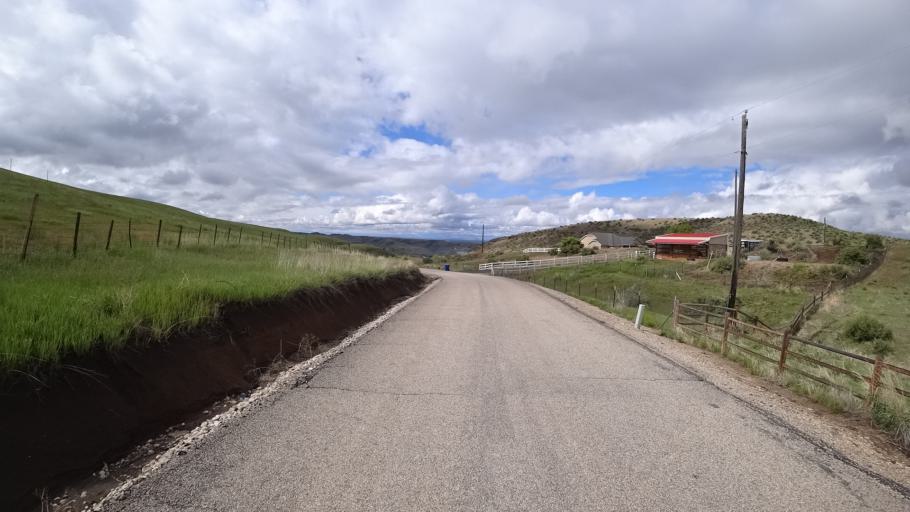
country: US
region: Idaho
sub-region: Ada County
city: Garden City
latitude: 43.7384
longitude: -116.2265
